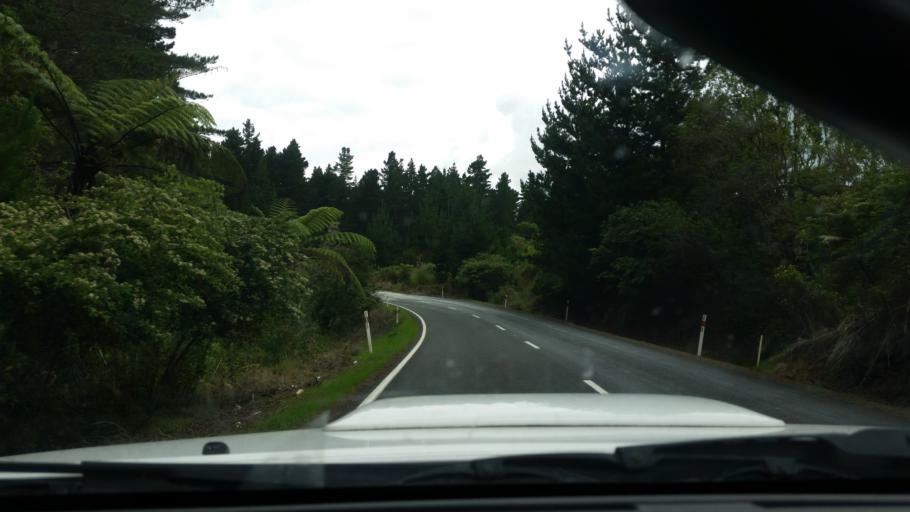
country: NZ
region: Northland
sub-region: Kaipara District
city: Dargaville
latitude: -35.7277
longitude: 173.8615
